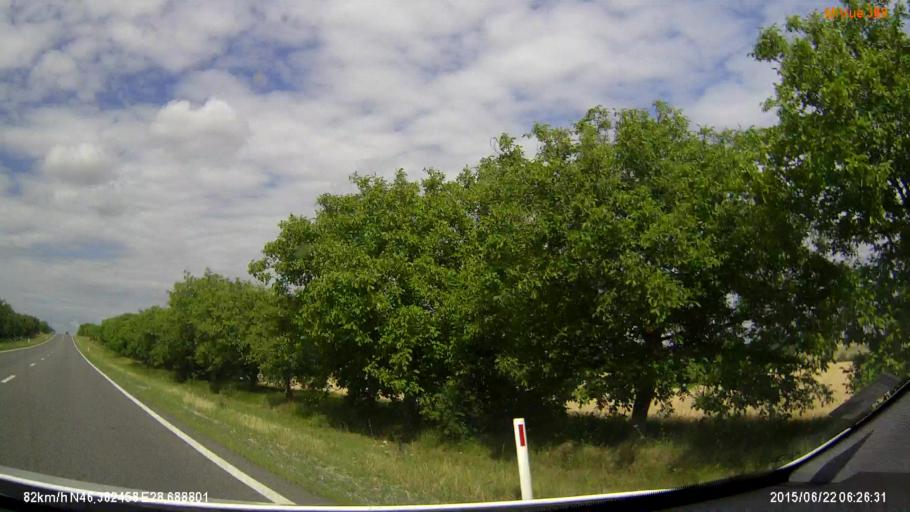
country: MD
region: Gagauzia
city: Bugeac
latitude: 46.3821
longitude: 28.6884
